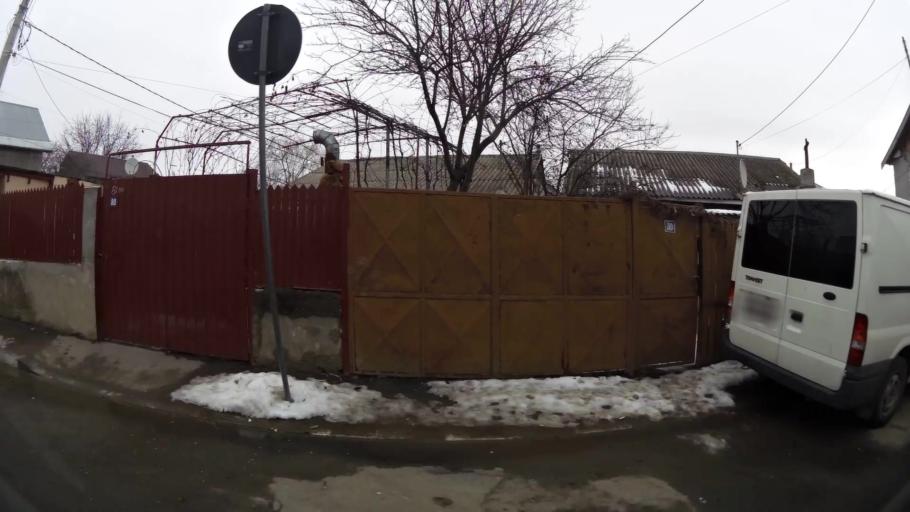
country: RO
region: Ilfov
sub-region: Comuna Pantelimon
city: Pantelimon
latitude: 44.4607
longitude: 26.2053
